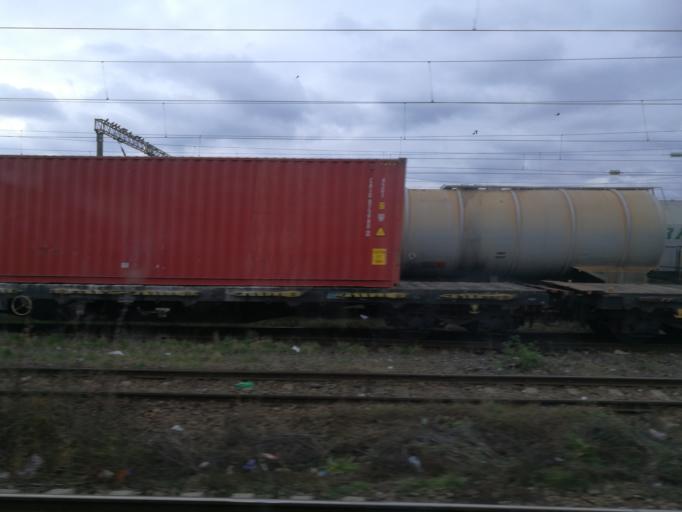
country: RO
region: Bacau
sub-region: Municipiul Bacau
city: Bacau
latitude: 46.5631
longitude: 26.8973
